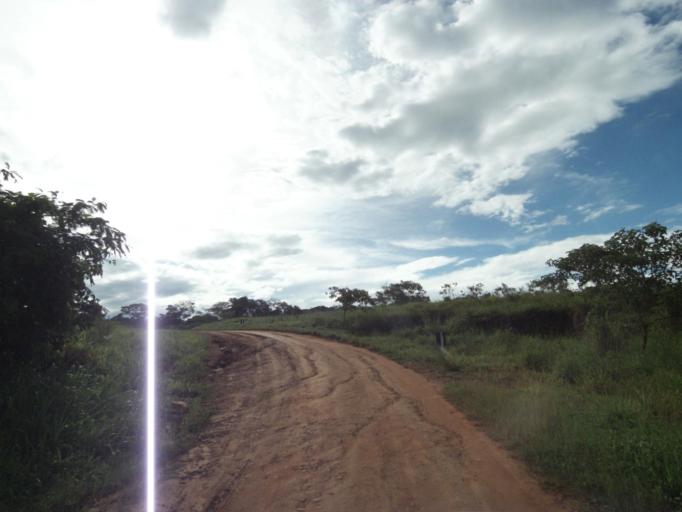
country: BR
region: Goias
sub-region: Jaragua
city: Jaragua
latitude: -15.8431
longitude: -49.3607
